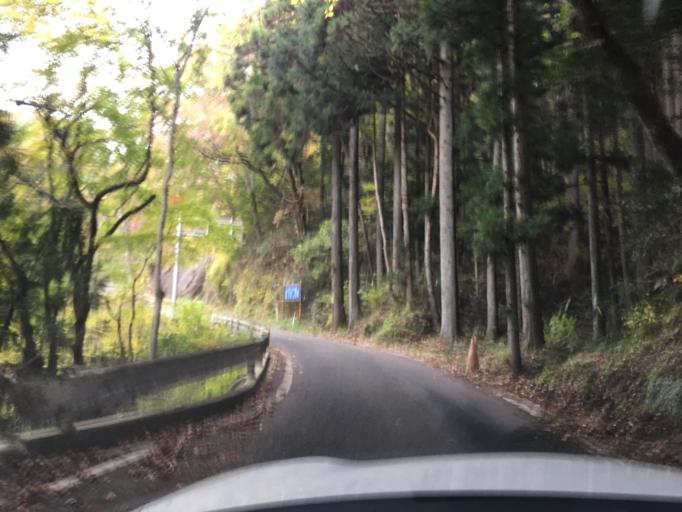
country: JP
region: Fukushima
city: Iwaki
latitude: 37.2052
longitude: 140.7623
